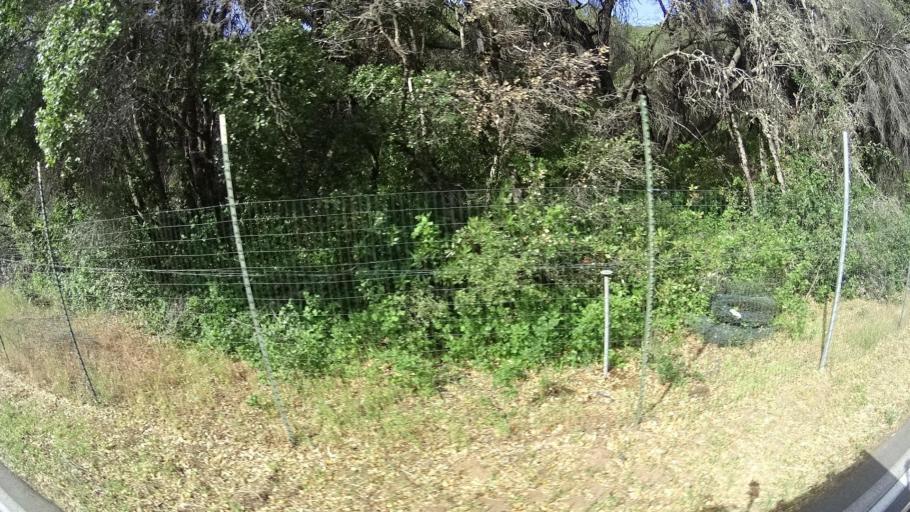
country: US
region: California
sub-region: Lake County
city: Soda Bay
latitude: 38.9692
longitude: -122.7399
